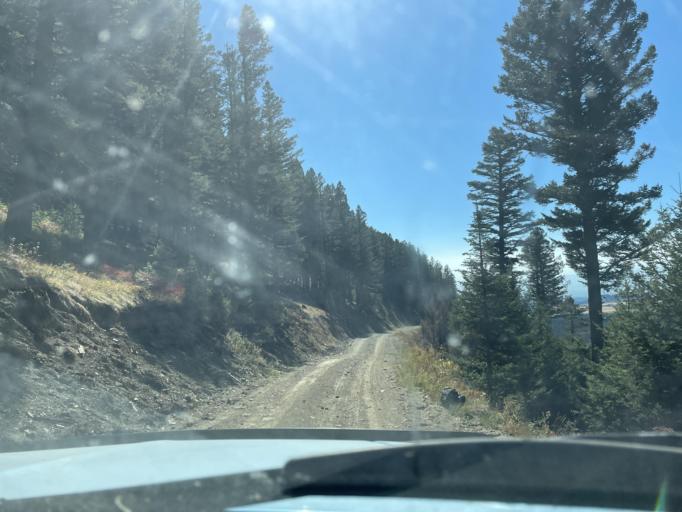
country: US
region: Montana
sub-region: Broadwater County
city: Townsend
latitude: 46.5082
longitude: -111.2841
